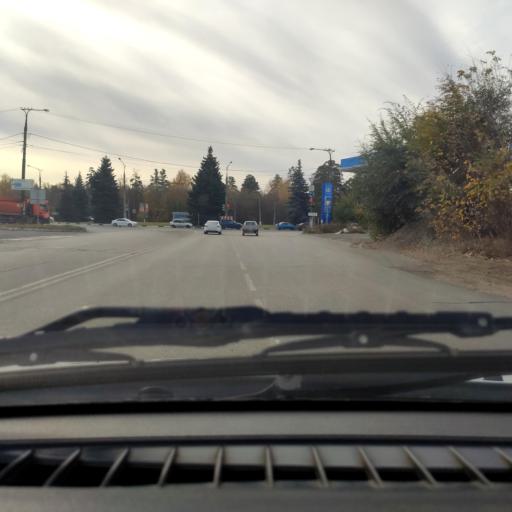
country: RU
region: Samara
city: Zhigulevsk
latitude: 53.5114
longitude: 49.4627
